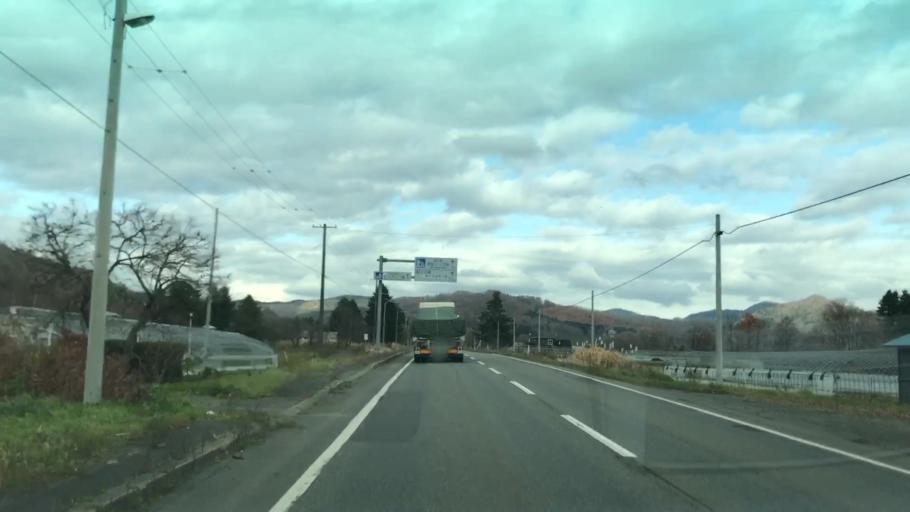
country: JP
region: Hokkaido
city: Shimo-furano
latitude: 42.8705
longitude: 142.4273
